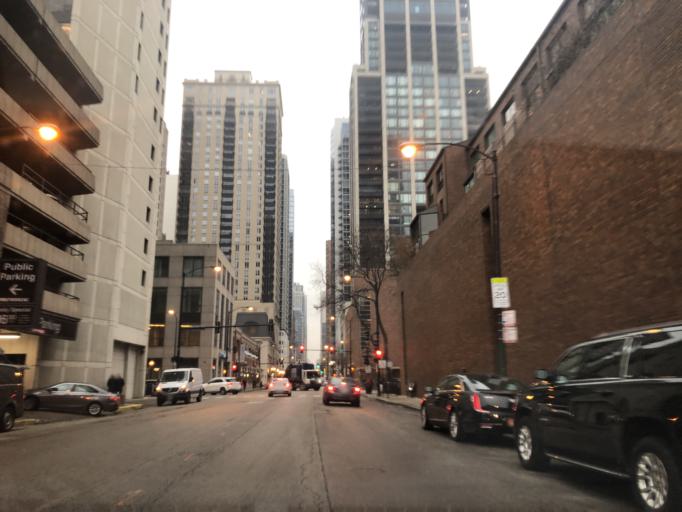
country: US
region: Illinois
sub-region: Cook County
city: Chicago
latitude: 41.9013
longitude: -87.6284
